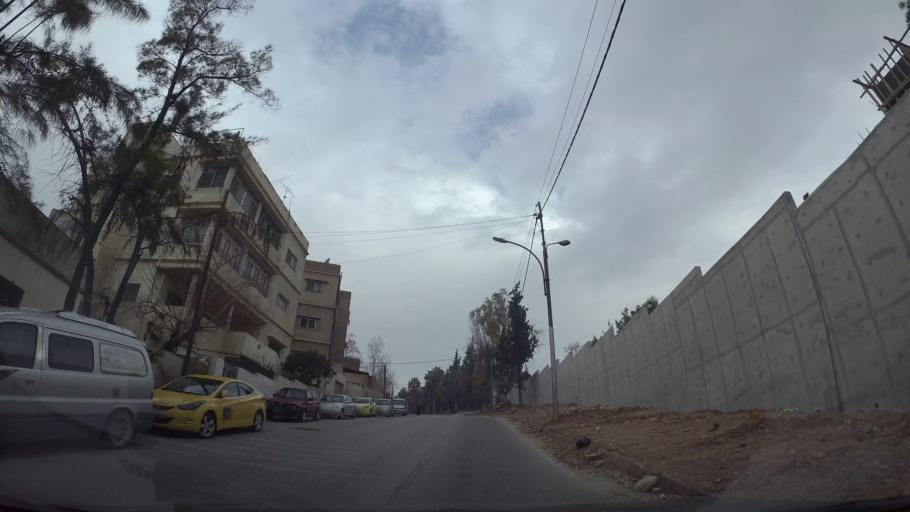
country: JO
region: Amman
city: Amman
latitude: 31.9572
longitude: 35.9444
